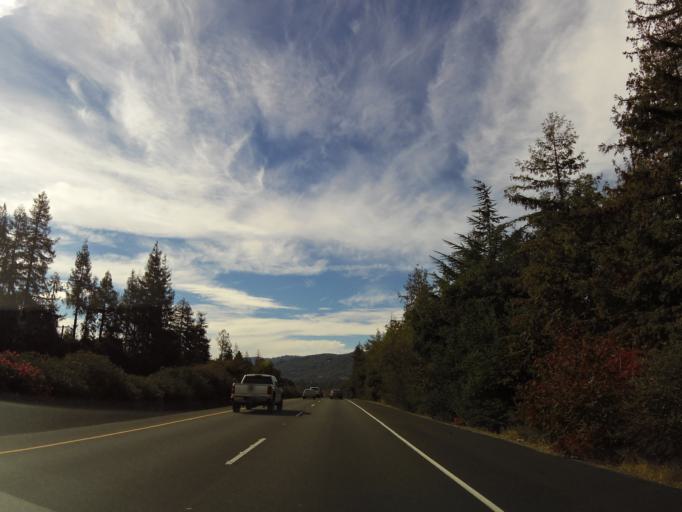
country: US
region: California
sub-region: Santa Clara County
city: Los Gatos
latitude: 37.2437
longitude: -121.9642
